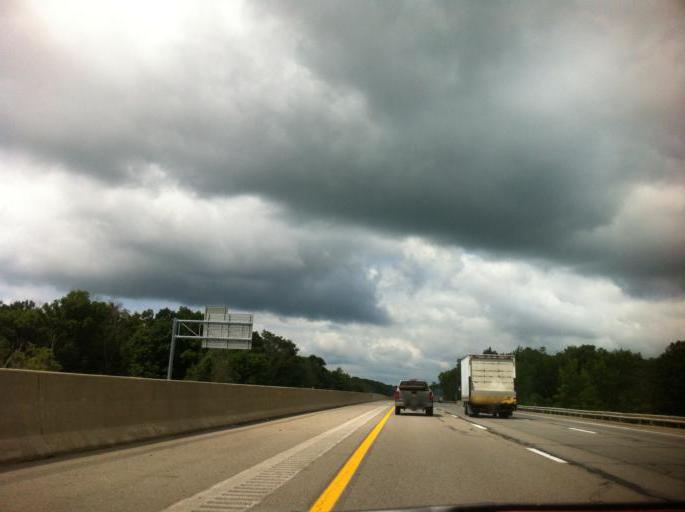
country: US
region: Ohio
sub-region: Portage County
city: Streetsboro
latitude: 41.2549
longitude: -81.3849
